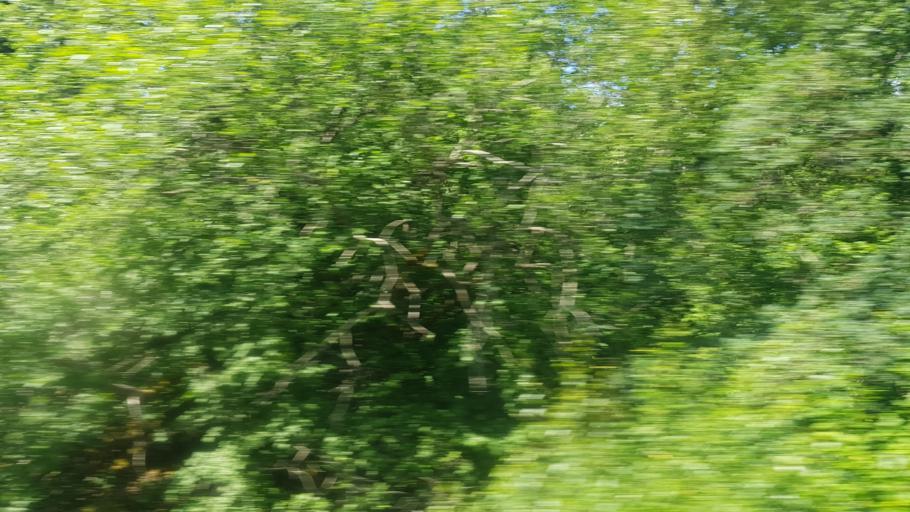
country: SE
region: Vaestra Goetaland
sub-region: Kungalvs Kommun
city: Kode
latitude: 57.9539
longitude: 11.8452
